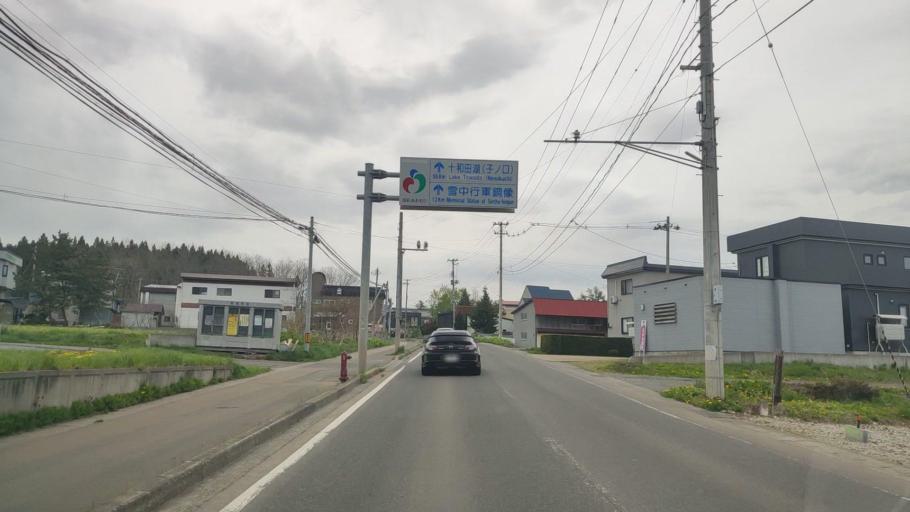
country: JP
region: Aomori
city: Aomori Shi
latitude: 40.7883
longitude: 140.7876
